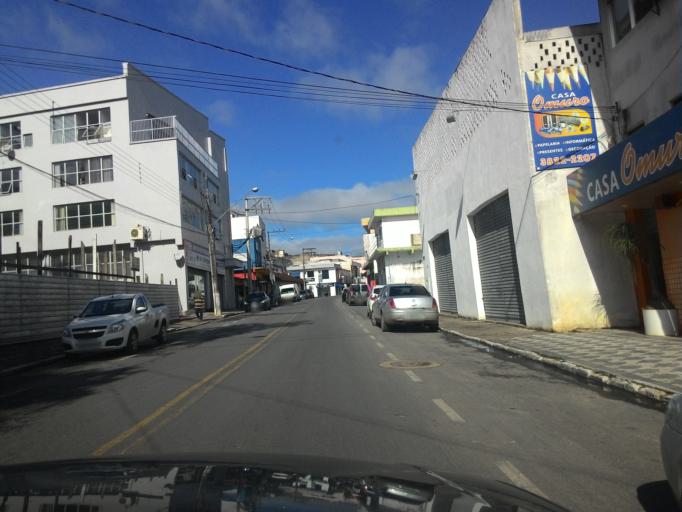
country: BR
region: Sao Paulo
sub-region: Registro
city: Registro
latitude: -24.4898
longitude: -47.8427
